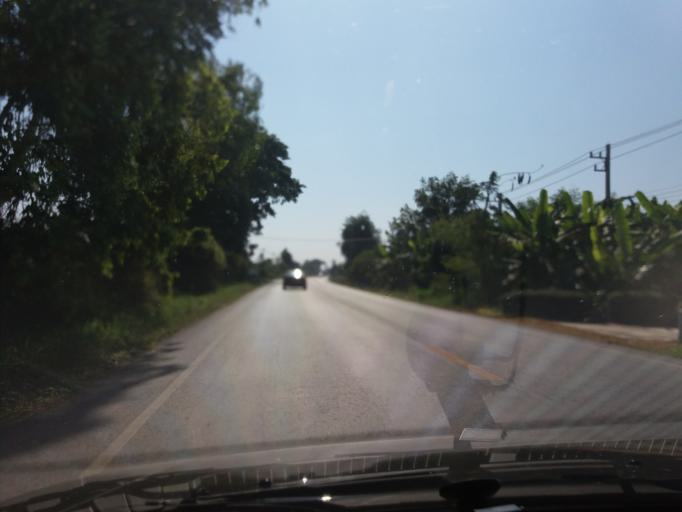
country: TH
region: Kamphaeng Phet
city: Khanu Woralaksaburi
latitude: 16.0672
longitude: 99.8671
